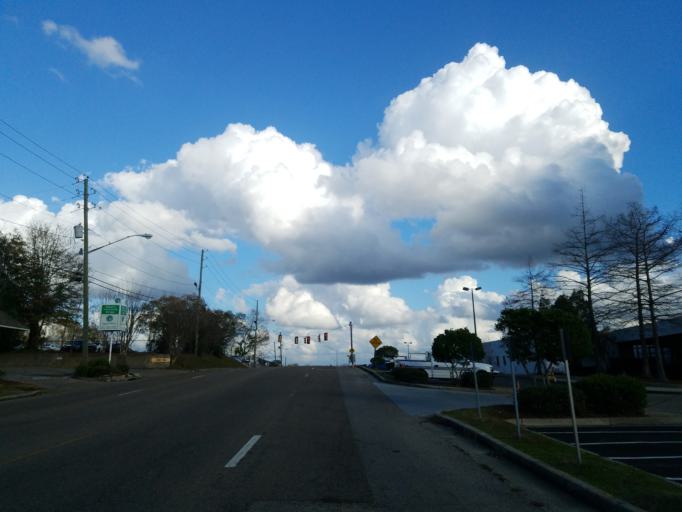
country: US
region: Mississippi
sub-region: Jones County
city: Laurel
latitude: 31.6859
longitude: -89.1411
